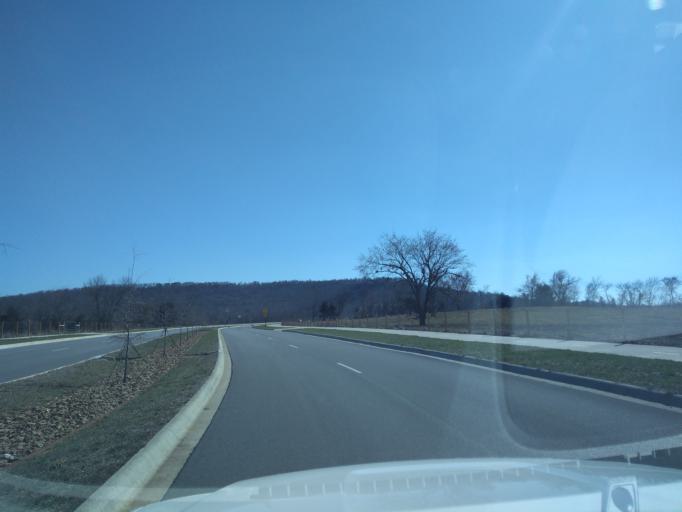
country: US
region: Arkansas
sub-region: Washington County
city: Farmington
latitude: 36.0549
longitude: -94.2204
